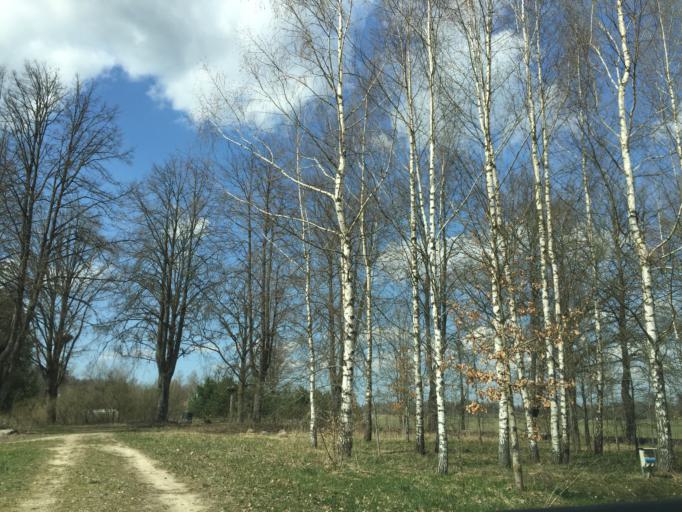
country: LV
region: Skriveri
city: Skriveri
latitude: 56.7469
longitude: 25.1088
